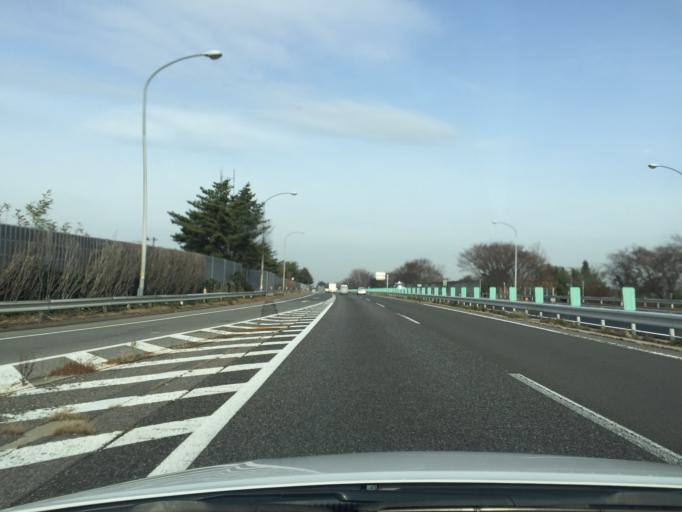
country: JP
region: Fukushima
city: Motomiya
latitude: 37.4893
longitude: 140.3778
